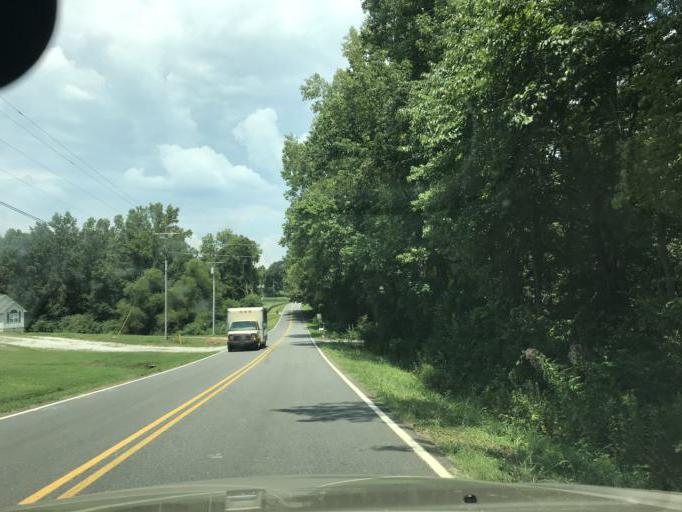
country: US
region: Georgia
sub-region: Dawson County
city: Dawsonville
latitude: 34.3216
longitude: -84.1700
